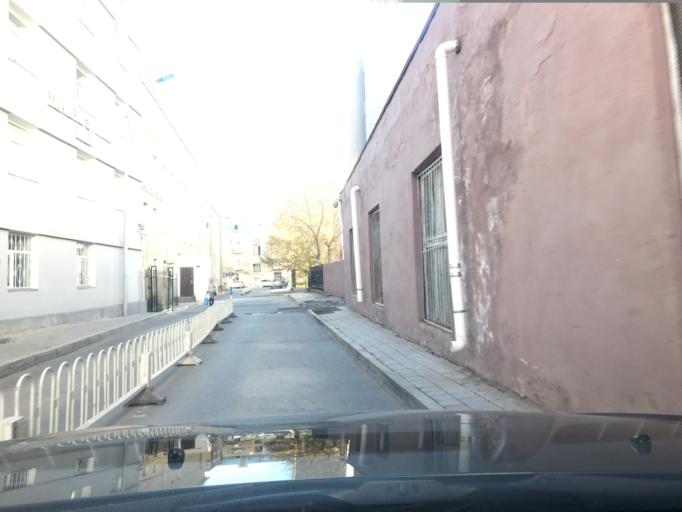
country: MN
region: Ulaanbaatar
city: Ulaanbaatar
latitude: 47.9212
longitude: 106.9134
